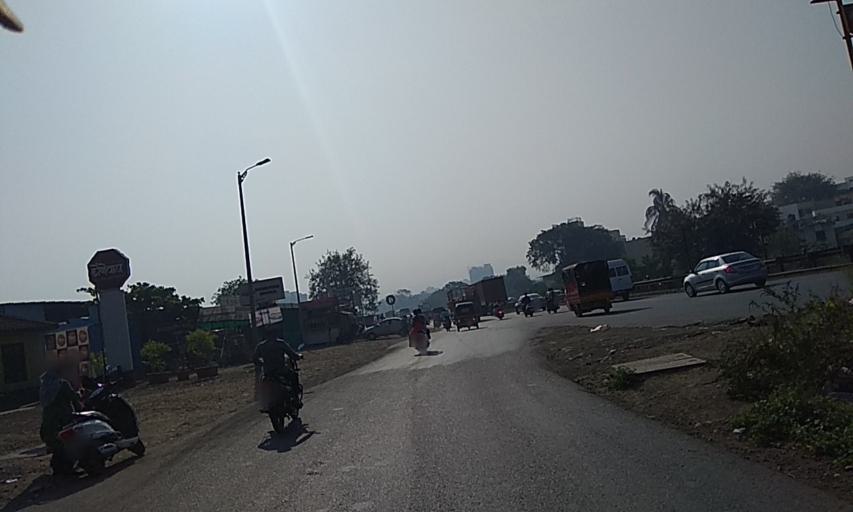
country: IN
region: Maharashtra
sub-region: Pune Division
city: Kharakvasla
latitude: 18.4780
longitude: 73.8066
